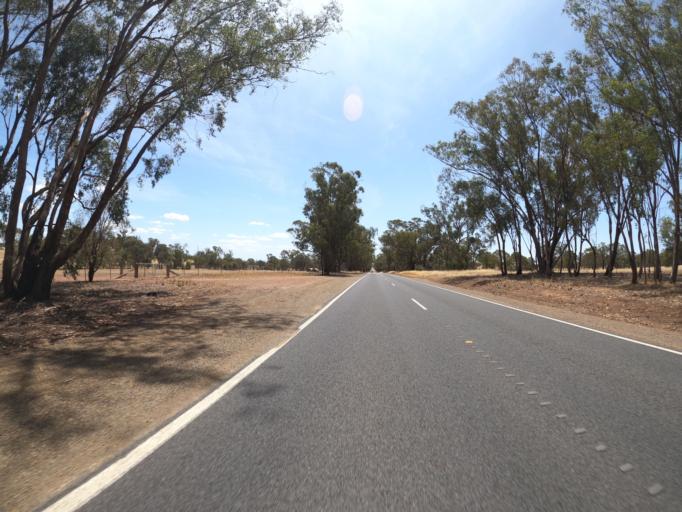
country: AU
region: Victoria
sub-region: Benalla
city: Benalla
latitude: -36.3618
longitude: 145.9680
